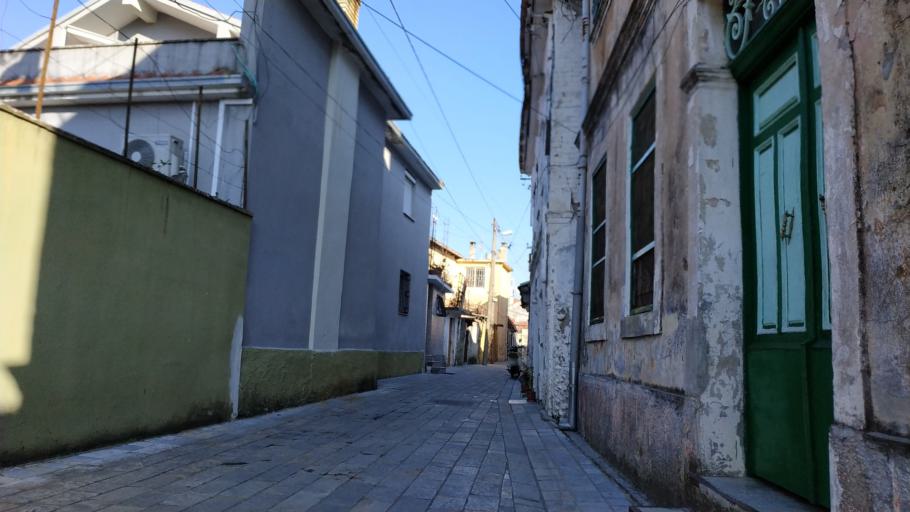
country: AL
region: Shkoder
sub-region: Rrethi i Shkodres
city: Shkoder
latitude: 42.0687
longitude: 19.5189
